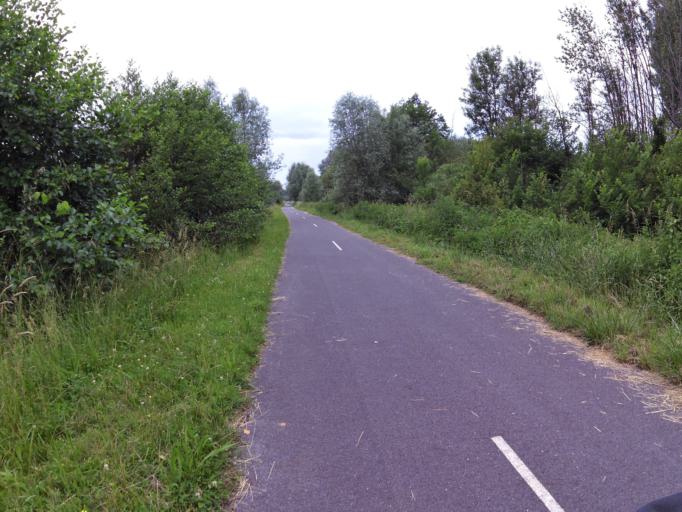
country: FR
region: Champagne-Ardenne
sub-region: Departement des Ardennes
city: Saint-Laurent
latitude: 49.7484
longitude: 4.7718
